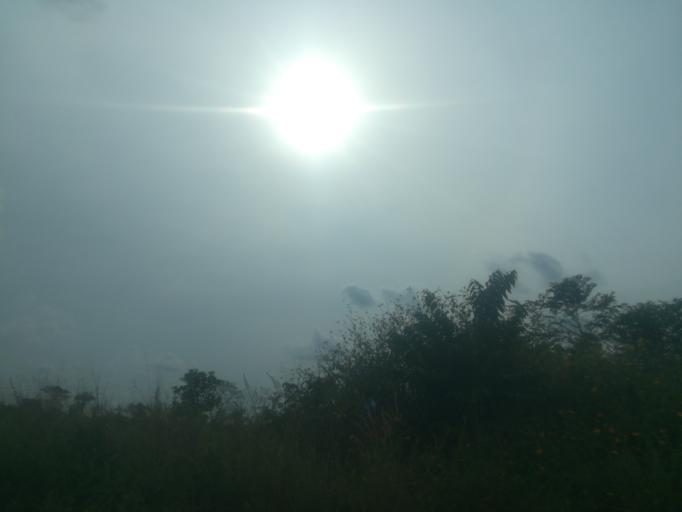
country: NG
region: Ogun
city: Ayetoro
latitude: 7.3197
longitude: 3.0686
